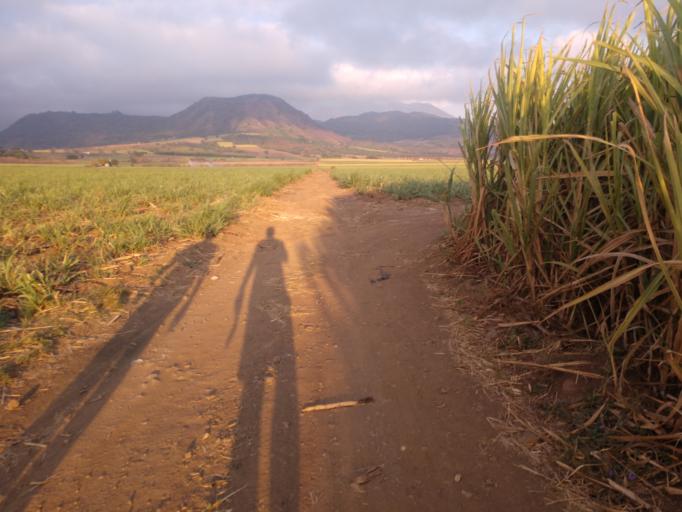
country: MX
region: Nayarit
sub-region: Tepic
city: La Corregidora
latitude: 21.4847
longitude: -104.8076
